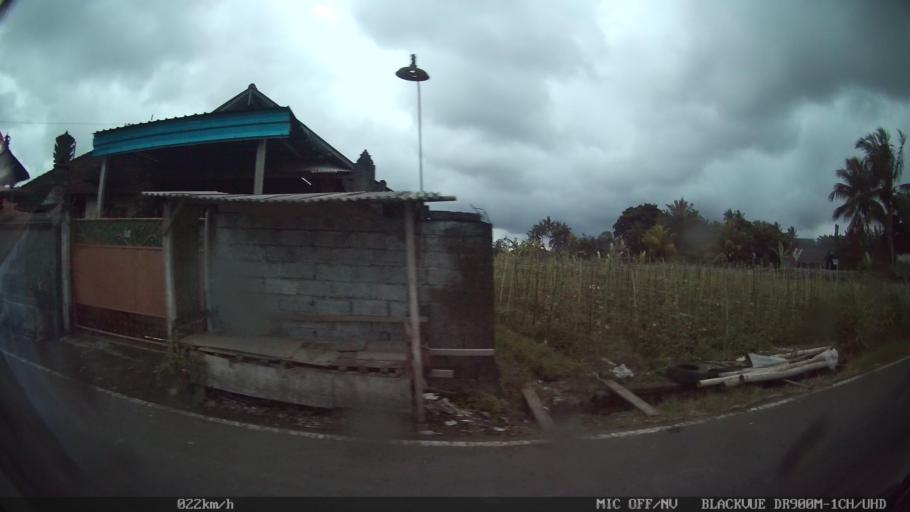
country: ID
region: Bali
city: Banjar Cemenggon
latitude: -8.5275
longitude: 115.1896
